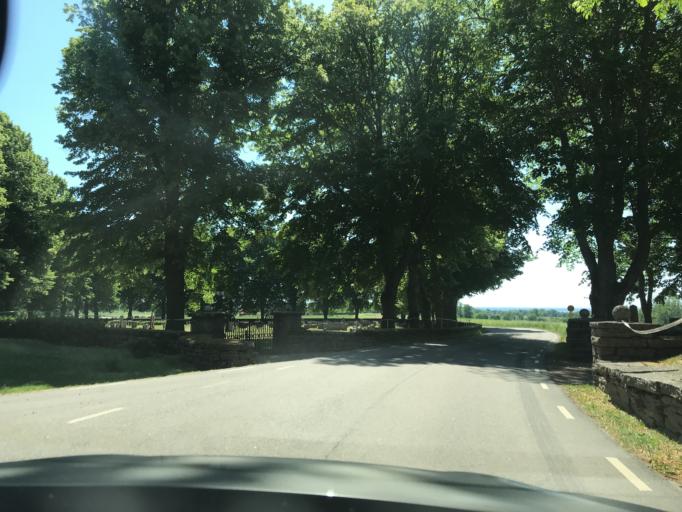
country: SE
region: Vaestra Goetaland
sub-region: Gotene Kommun
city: Kallby
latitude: 58.5780
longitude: 13.3722
